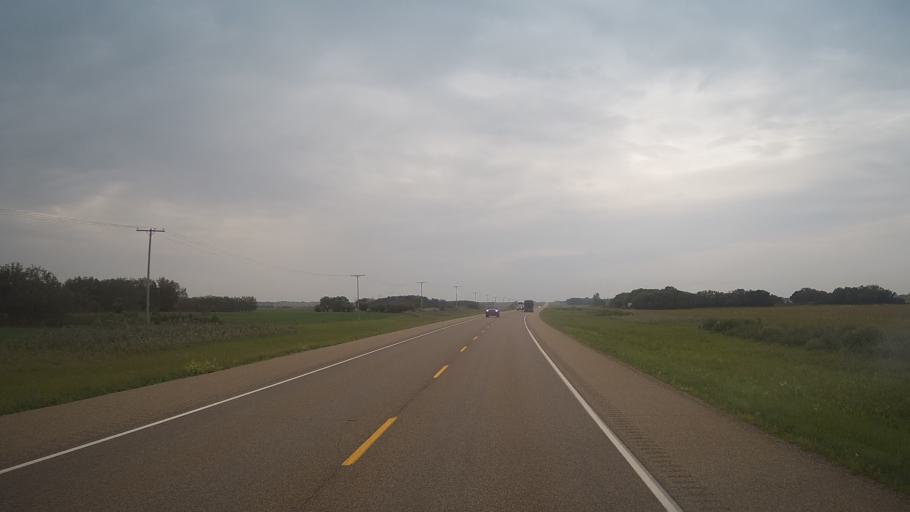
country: CA
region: Saskatchewan
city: Langham
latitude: 52.1290
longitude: -107.1135
